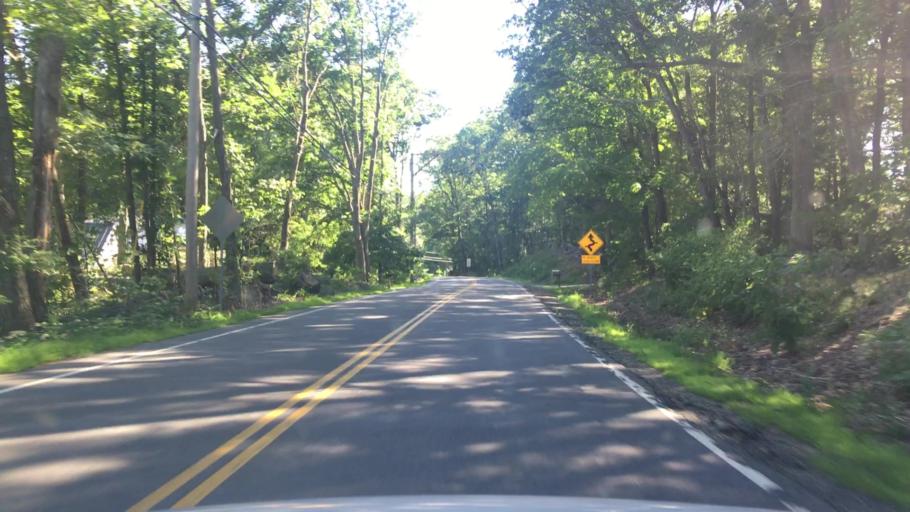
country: US
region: New Hampshire
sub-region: Rockingham County
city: Newmarket
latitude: 43.0357
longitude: -70.9540
